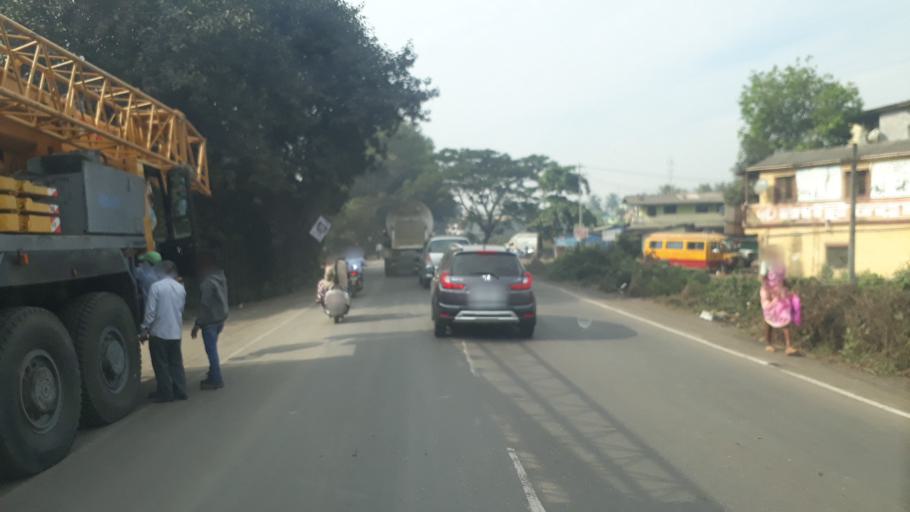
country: IN
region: Maharashtra
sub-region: Raigarh
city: Pen
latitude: 18.7152
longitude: 73.0579
